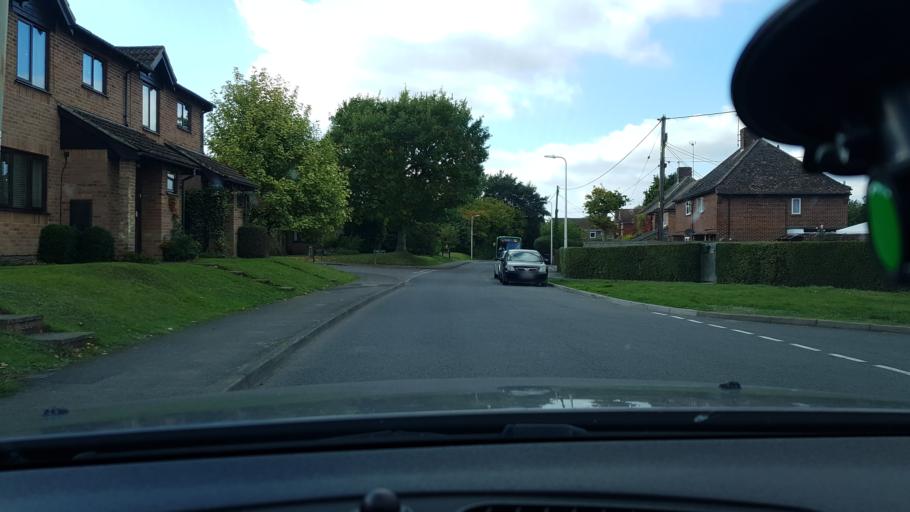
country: GB
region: England
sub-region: West Berkshire
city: Hungerford
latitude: 51.4061
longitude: -1.5156
